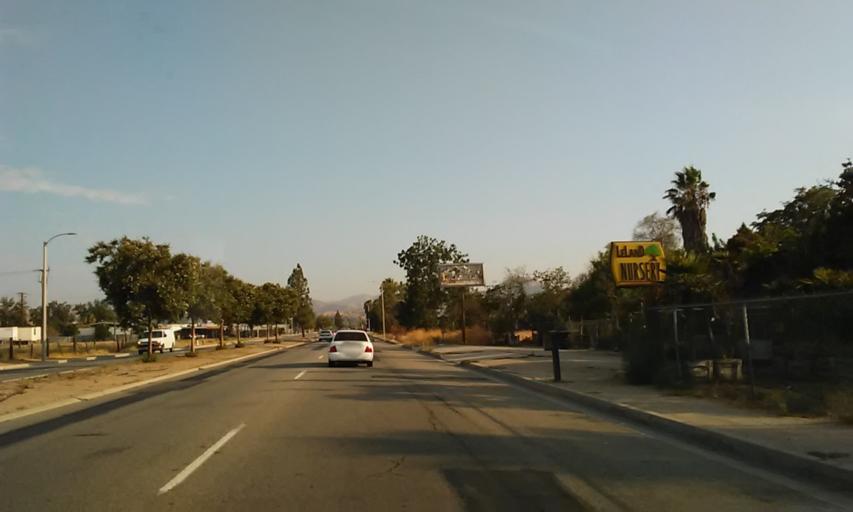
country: US
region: California
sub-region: San Bernardino County
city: San Bernardino
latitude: 34.0832
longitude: -117.2788
